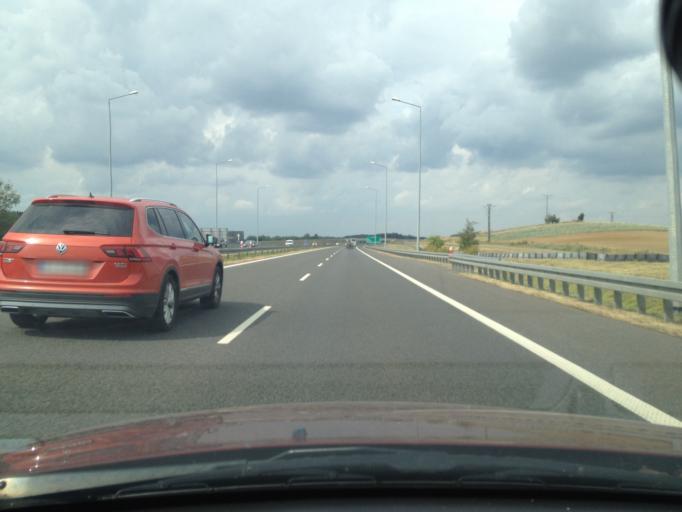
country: PL
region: West Pomeranian Voivodeship
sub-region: Powiat pyrzycki
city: Lipiany
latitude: 52.9552
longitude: 14.9400
